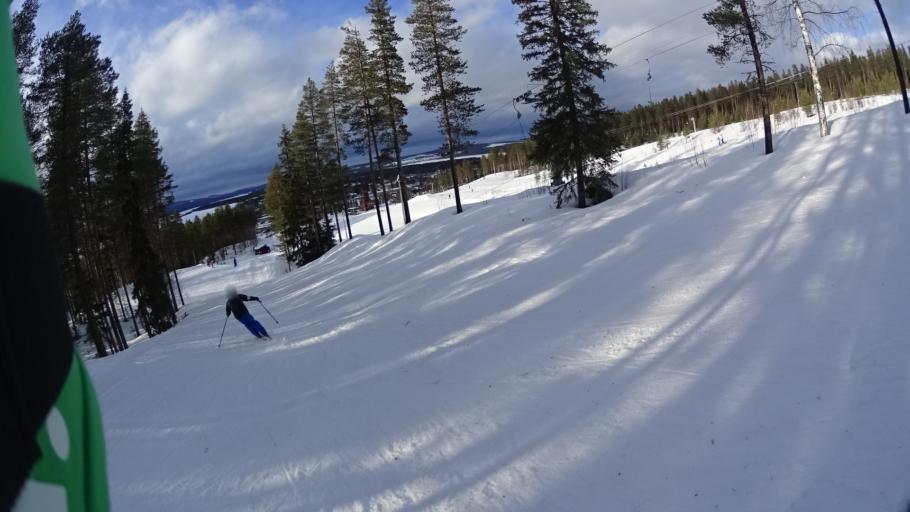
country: SE
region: Vaesterbotten
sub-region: Mala Kommun
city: Mala
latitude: 65.1785
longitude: 18.7566
